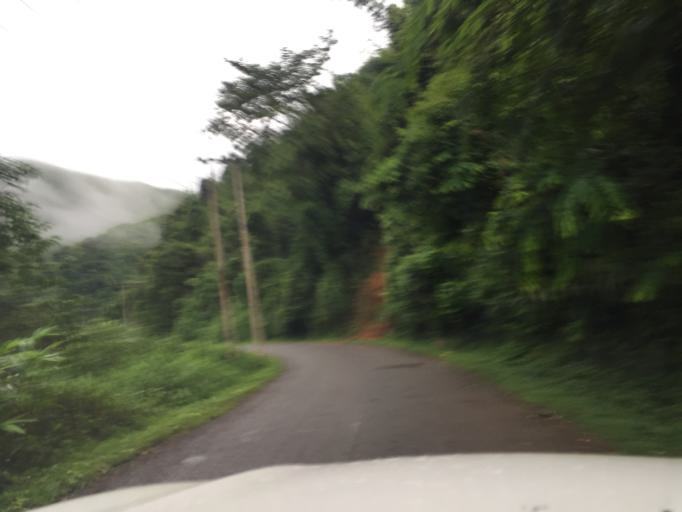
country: LA
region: Oudomxai
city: Muang La
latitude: 20.9415
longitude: 102.2072
